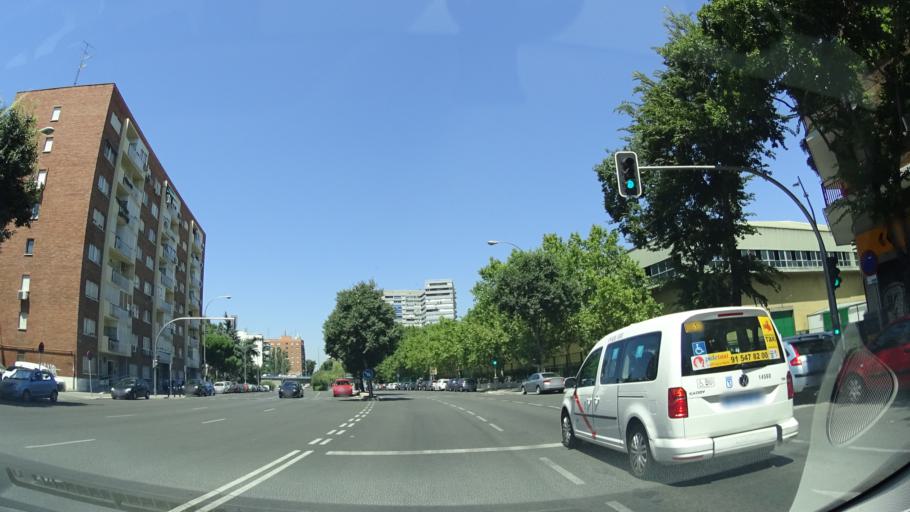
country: ES
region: Madrid
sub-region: Provincia de Madrid
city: Usera
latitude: 40.3921
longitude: -3.7039
